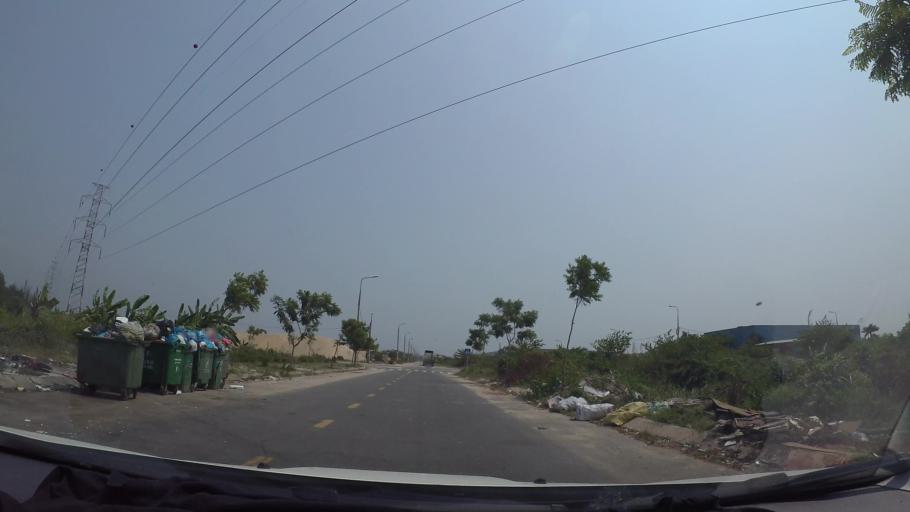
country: VN
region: Da Nang
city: Cam Le
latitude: 15.9932
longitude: 108.1967
